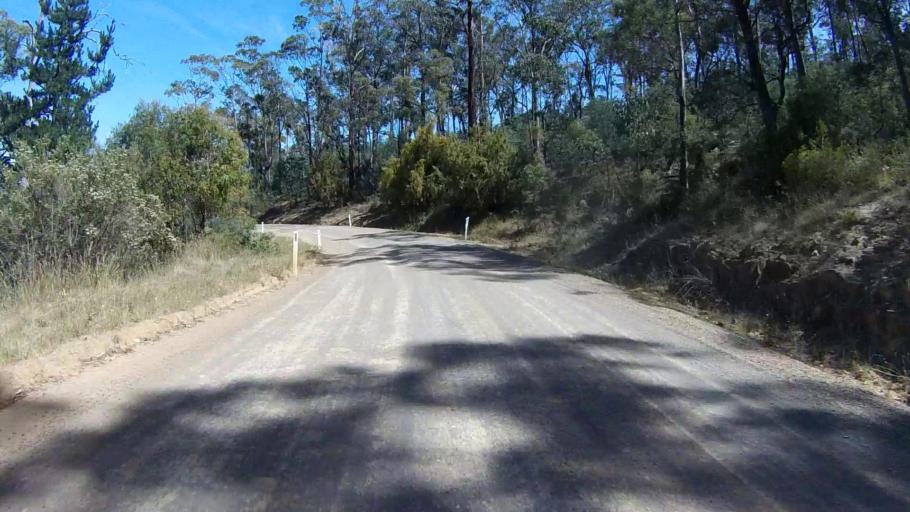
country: AU
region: Tasmania
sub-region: Sorell
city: Sorell
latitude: -42.7583
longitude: 147.6765
